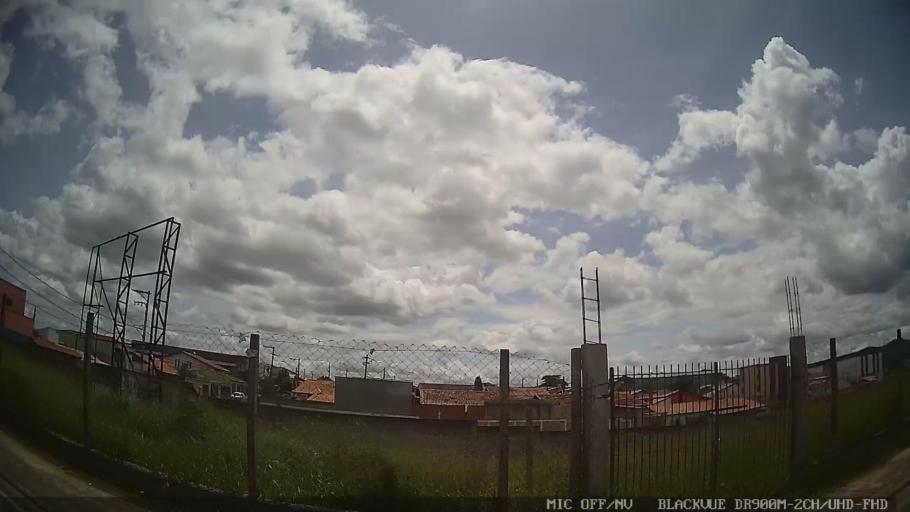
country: BR
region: Sao Paulo
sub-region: Mogi das Cruzes
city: Mogi das Cruzes
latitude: -23.5396
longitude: -46.2031
